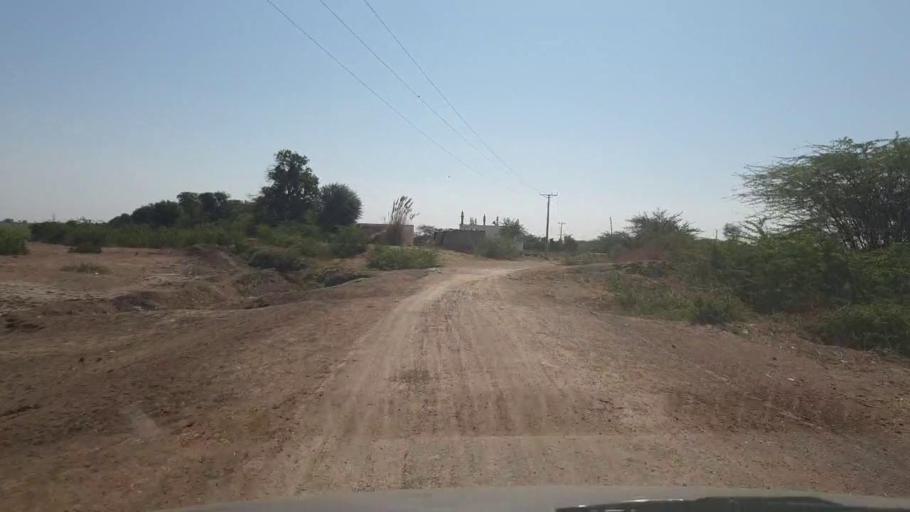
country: PK
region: Sindh
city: Umarkot
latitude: 25.3856
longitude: 69.6207
